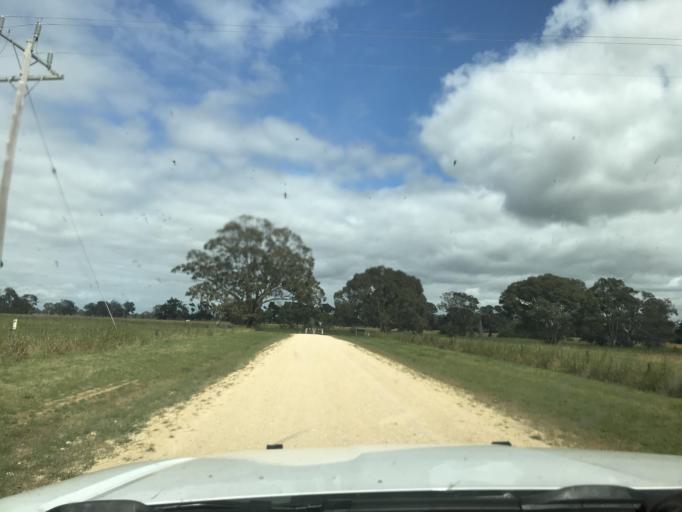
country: AU
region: South Australia
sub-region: Naracoorte and Lucindale
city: Naracoorte
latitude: -37.0513
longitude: 141.0517
